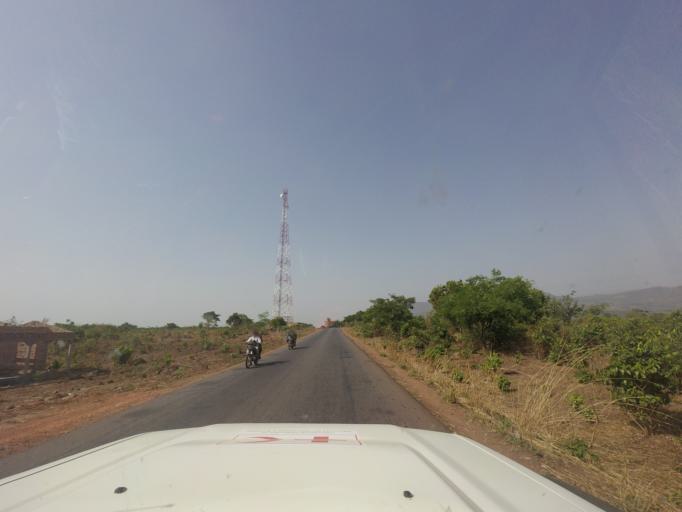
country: GN
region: Mamou
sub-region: Mamou Prefecture
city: Mamou
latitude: 10.2594
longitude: -12.4561
